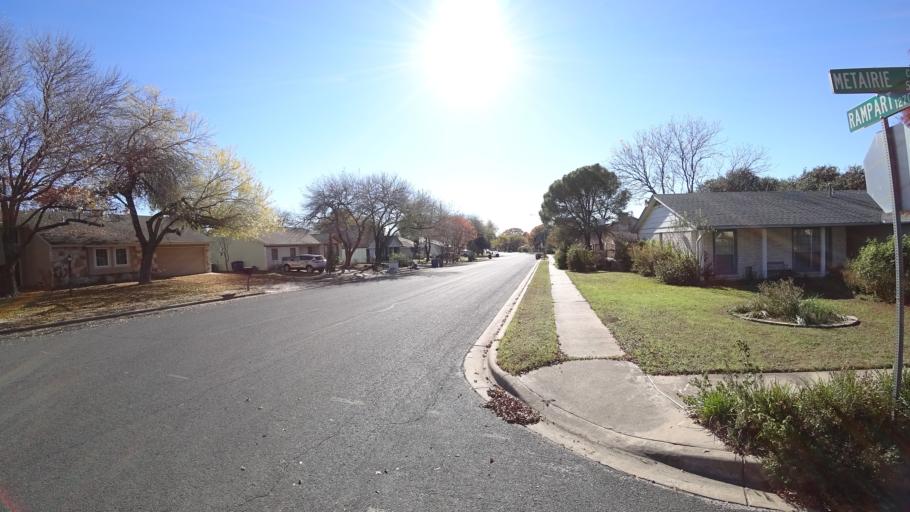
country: US
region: Texas
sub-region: Travis County
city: Wells Branch
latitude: 30.4182
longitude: -97.6907
